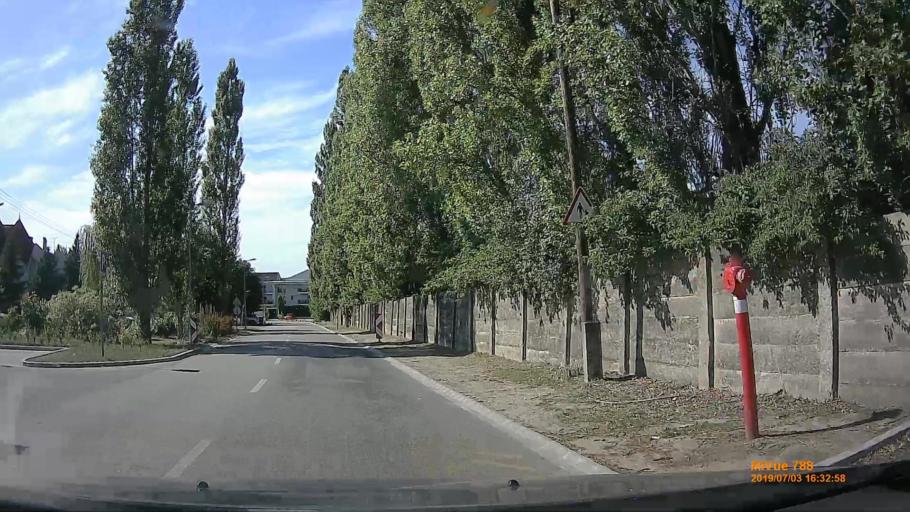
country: HU
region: Gyor-Moson-Sopron
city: Gyor
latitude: 47.7031
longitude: 17.6372
